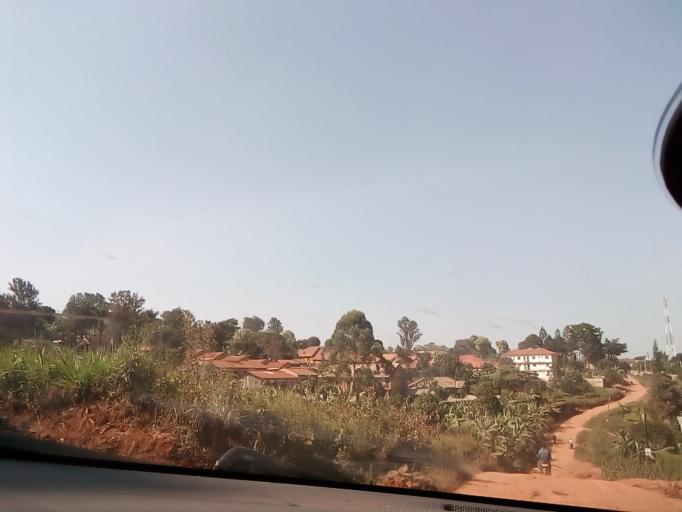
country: UG
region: Central Region
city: Masaka
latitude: -0.3407
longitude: 31.7315
